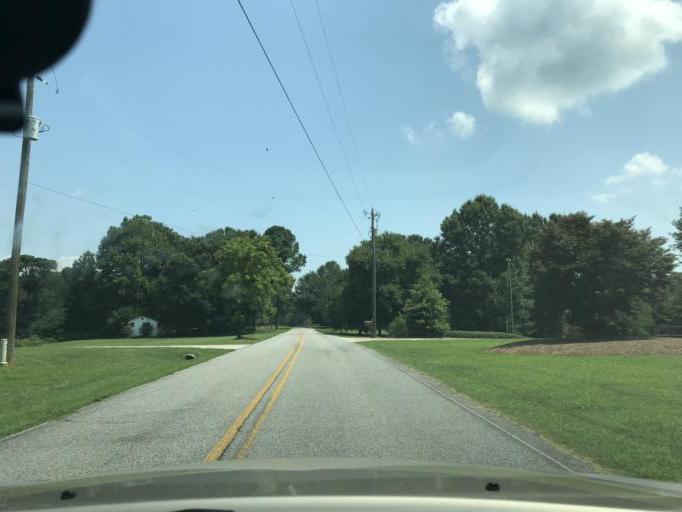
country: US
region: Georgia
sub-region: Dawson County
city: Dawsonville
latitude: 34.3244
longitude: -84.0905
